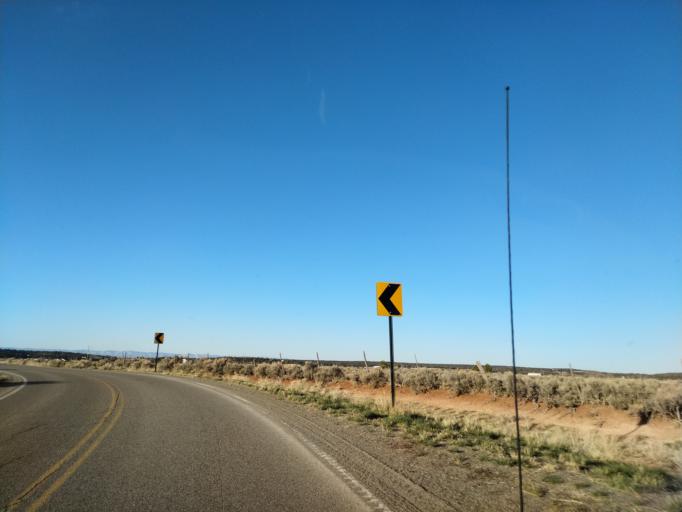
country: US
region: Colorado
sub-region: Mesa County
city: Redlands
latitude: 38.9905
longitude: -108.7510
